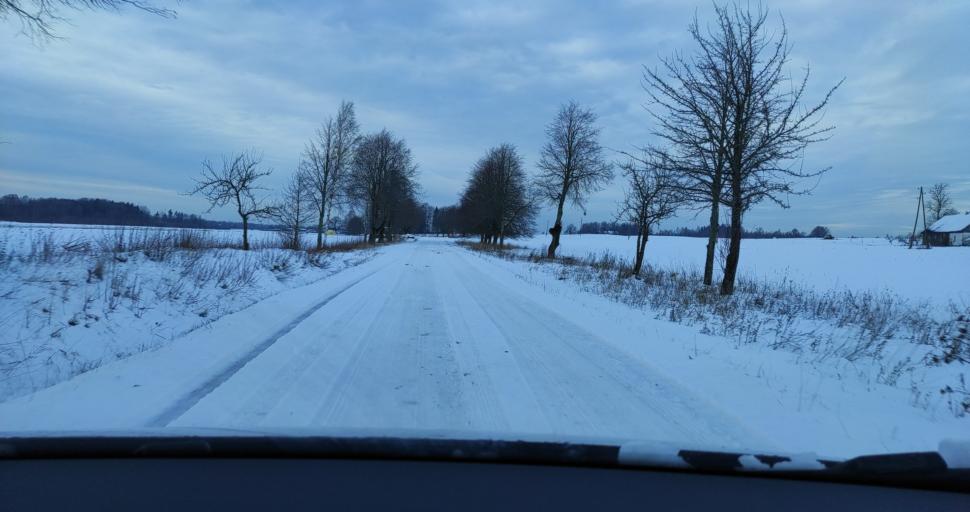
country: LV
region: Kuldigas Rajons
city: Kuldiga
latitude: 56.9446
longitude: 22.0264
